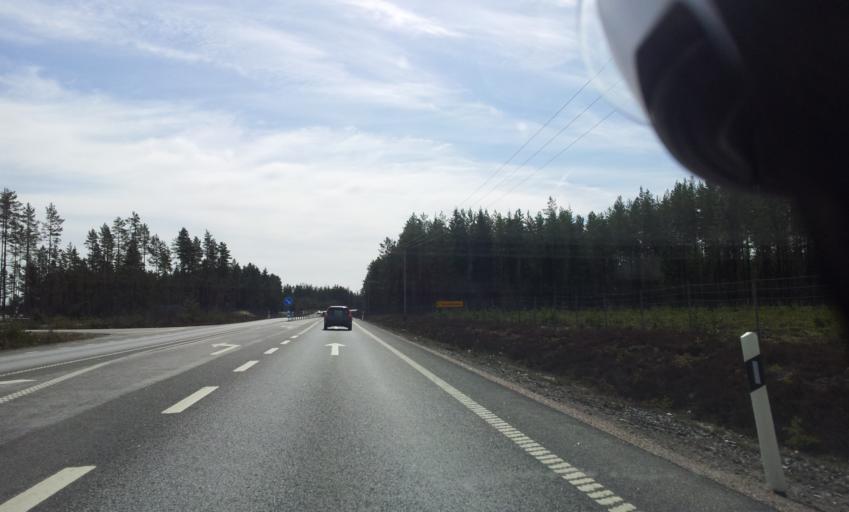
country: SE
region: Gaevleborg
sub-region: Gavle Kommun
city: Norrsundet
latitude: 61.0355
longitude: 16.9697
